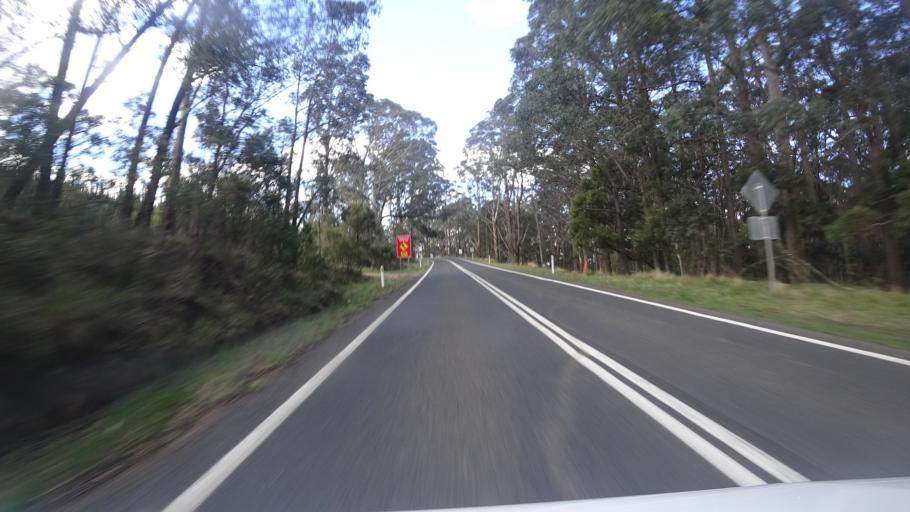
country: AU
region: New South Wales
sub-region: Lithgow
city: Bowenfels
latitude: -33.6715
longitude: 150.0509
